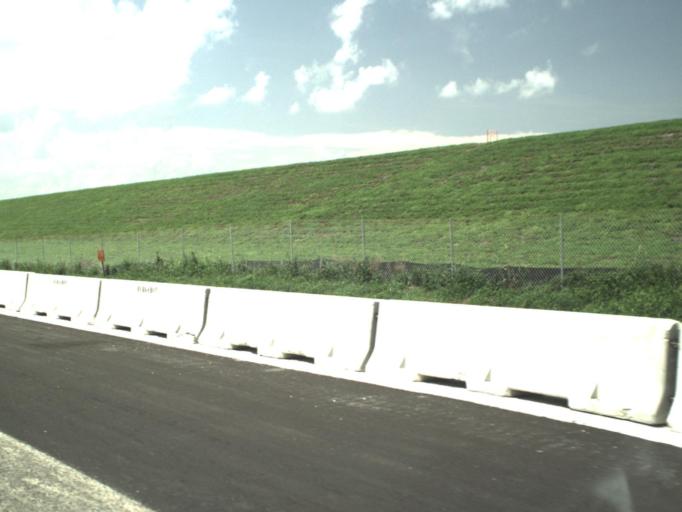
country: US
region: Florida
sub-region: Hendry County
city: Clewiston
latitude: 26.7233
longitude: -80.8470
